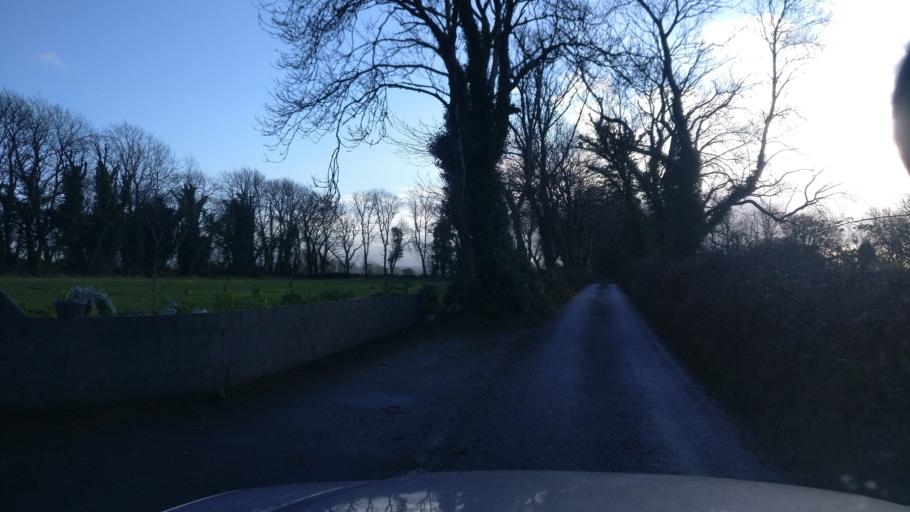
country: IE
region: Connaught
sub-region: County Galway
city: Loughrea
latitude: 53.2311
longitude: -8.5768
